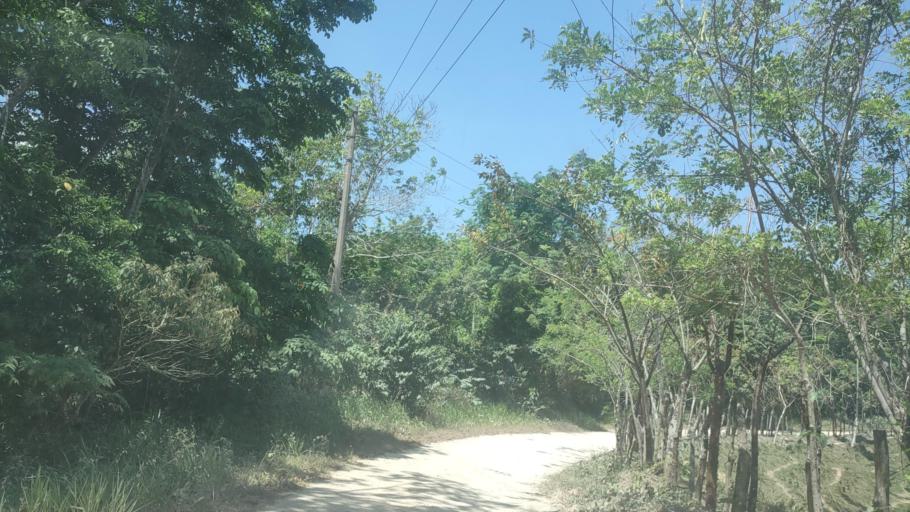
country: MX
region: Veracruz
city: Las Choapas
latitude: 17.7883
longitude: -94.1518
